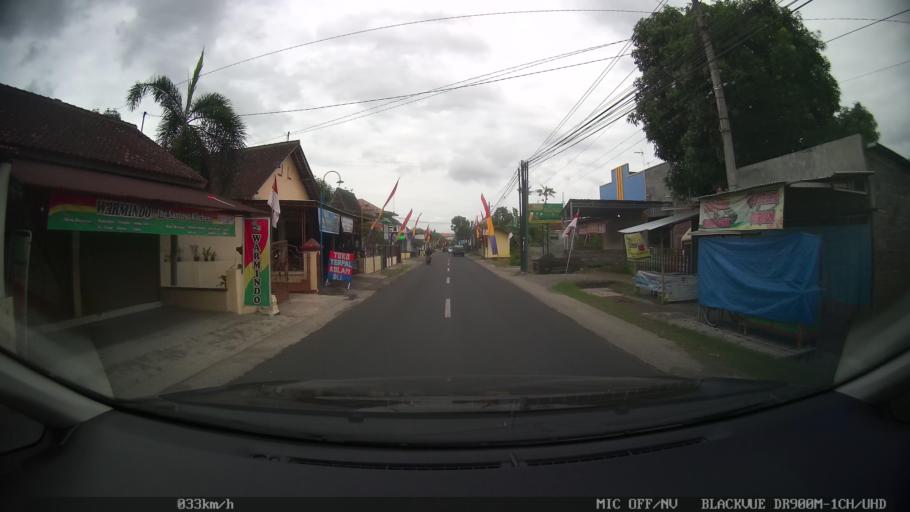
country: ID
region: Daerah Istimewa Yogyakarta
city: Sewon
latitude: -7.8589
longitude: 110.4091
